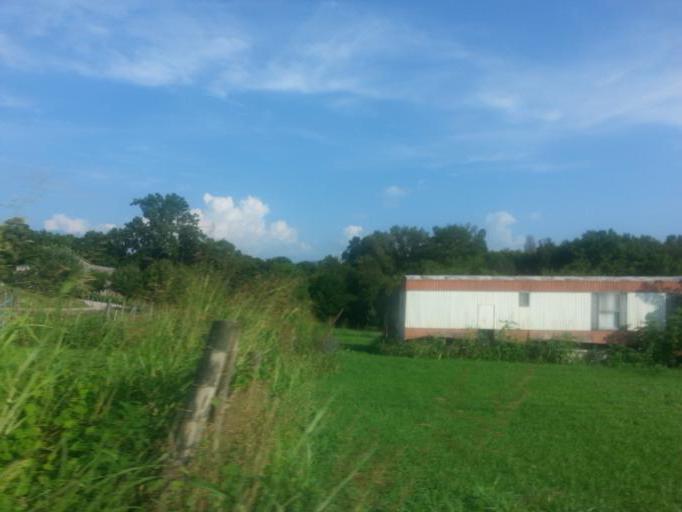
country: US
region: Tennessee
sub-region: Blount County
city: Wildwood
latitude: 35.8236
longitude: -83.8145
